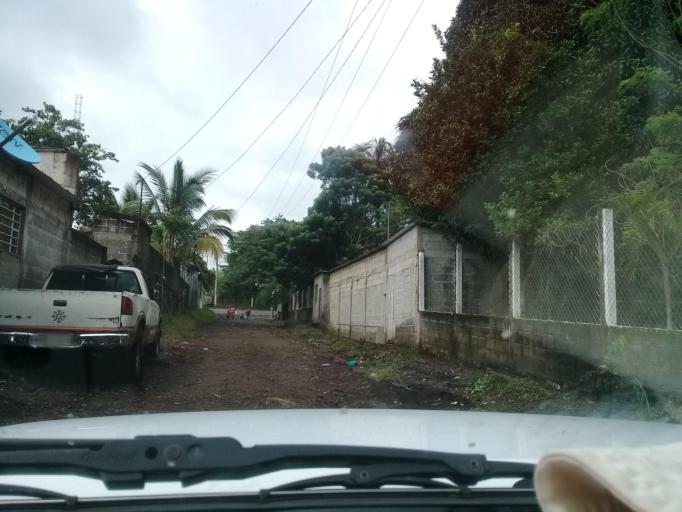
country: MX
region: Veracruz
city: Catemaco
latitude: 18.4302
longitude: -95.1303
